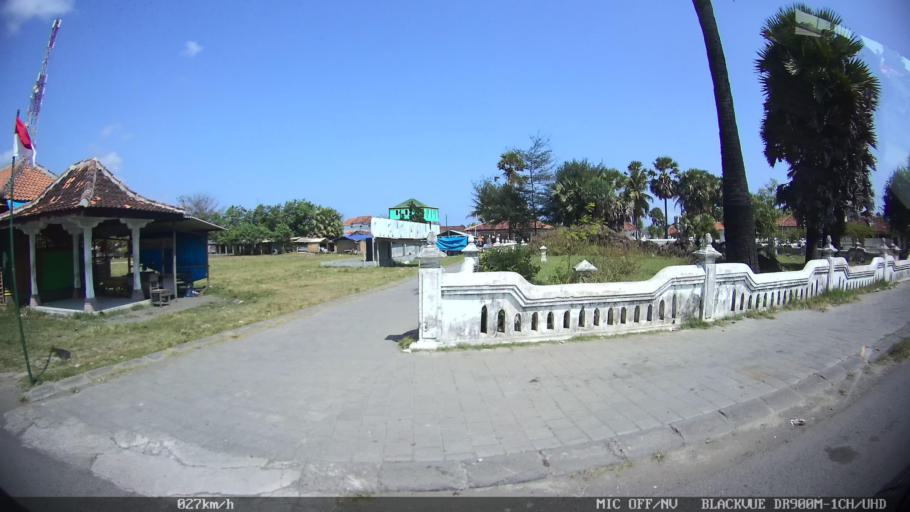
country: ID
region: Daerah Istimewa Yogyakarta
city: Pundong
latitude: -8.0201
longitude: 110.3254
